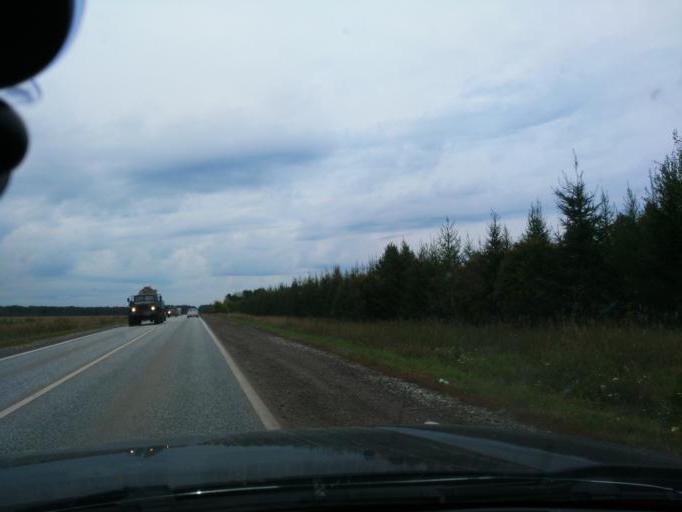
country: RU
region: Perm
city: Chernushka
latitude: 56.6085
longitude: 56.1601
